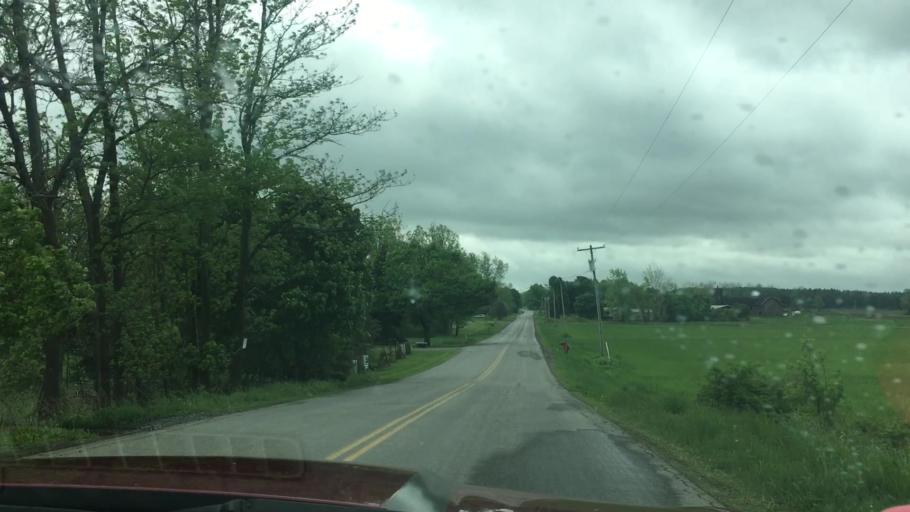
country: US
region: New York
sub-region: Genesee County
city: Batavia
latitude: 43.0791
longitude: -78.1396
